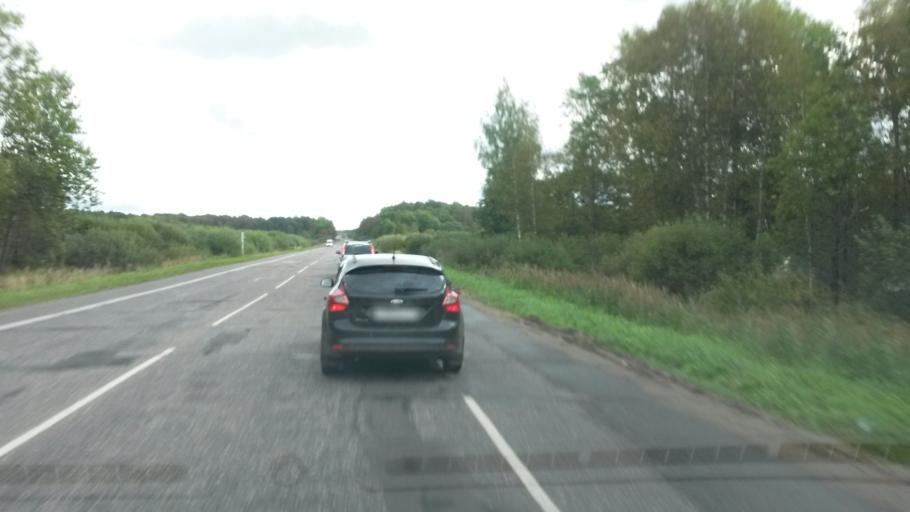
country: RU
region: Ivanovo
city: Rodniki
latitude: 57.0864
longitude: 41.6176
